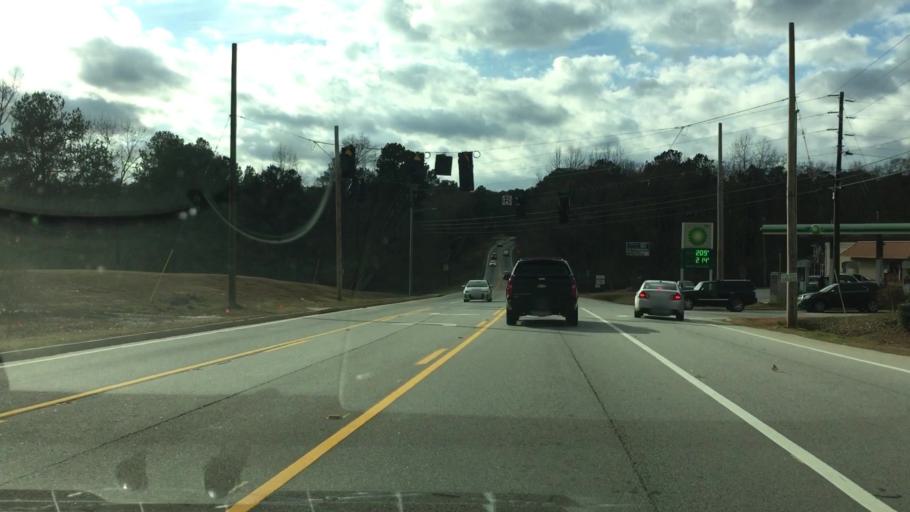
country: US
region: Georgia
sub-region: Henry County
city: McDonough
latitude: 33.4349
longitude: -84.1646
